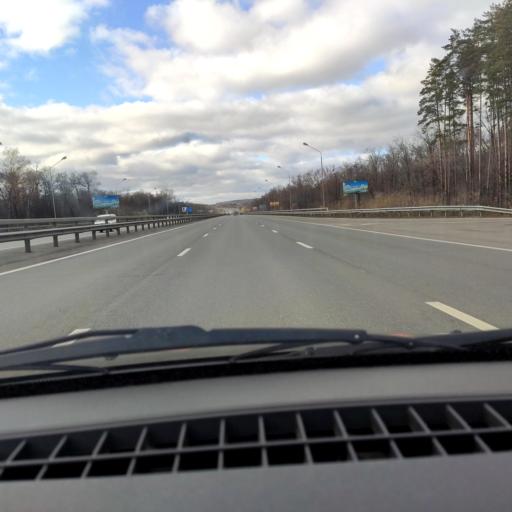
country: RU
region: Bashkortostan
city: Avdon
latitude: 54.6716
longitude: 55.8386
